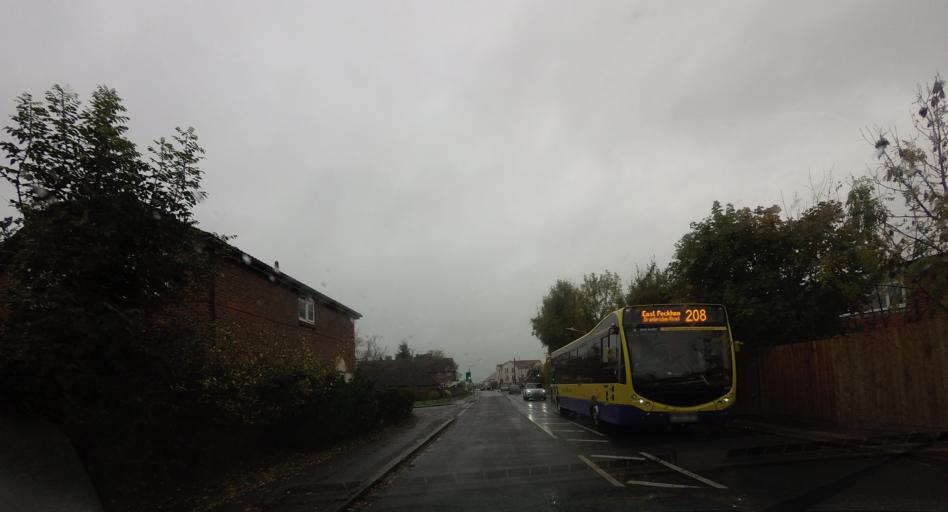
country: GB
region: England
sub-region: Kent
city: Tonbridge
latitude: 51.2092
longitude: 0.2805
